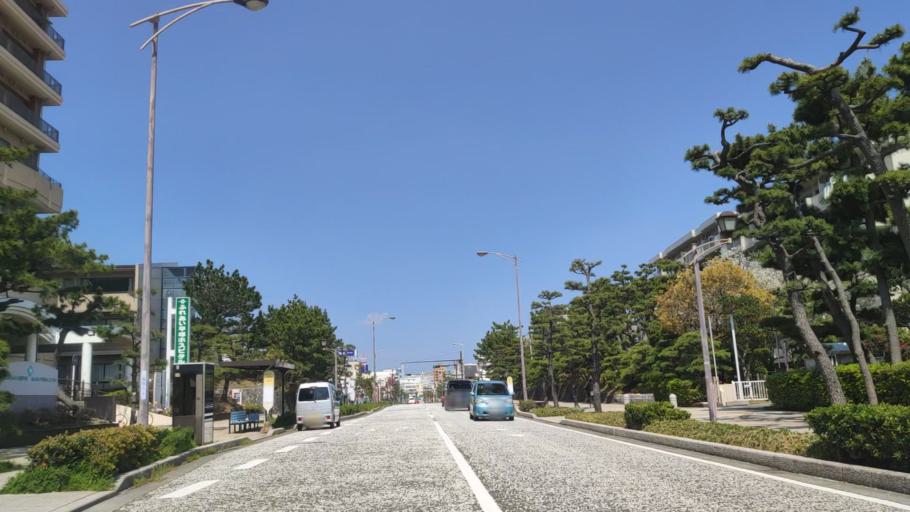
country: JP
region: Kanagawa
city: Hiratsuka
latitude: 35.3192
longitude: 139.3534
